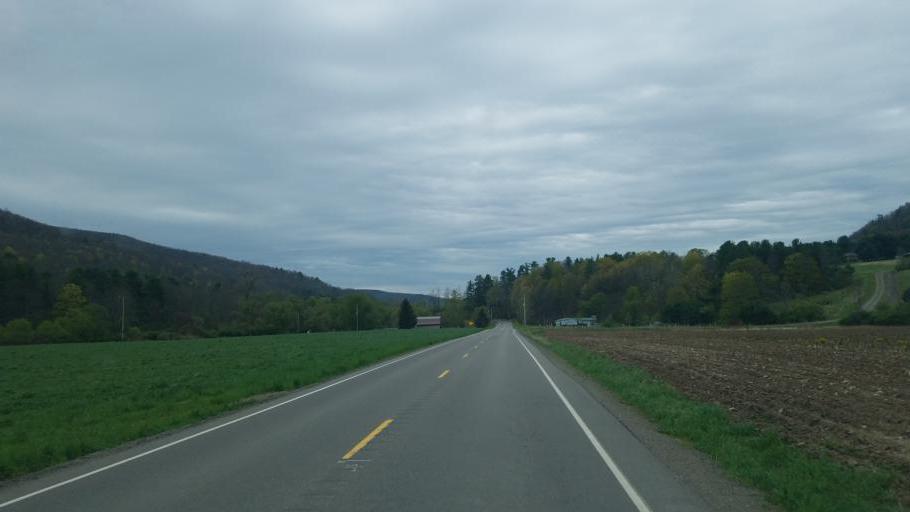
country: US
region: Pennsylvania
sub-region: Tioga County
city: Westfield
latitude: 41.9704
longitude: -77.4558
